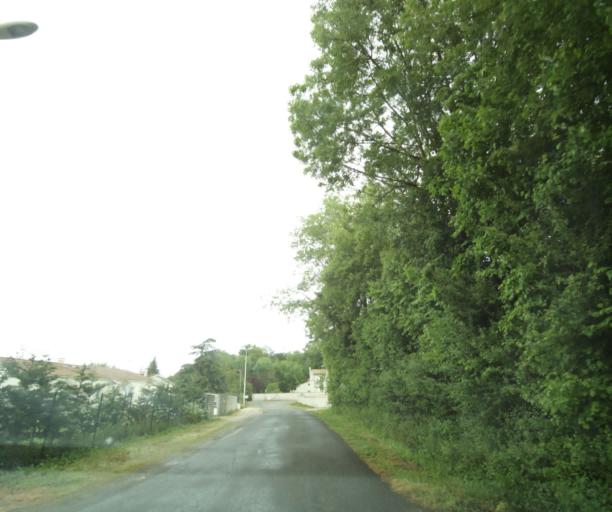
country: FR
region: Poitou-Charentes
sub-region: Departement de la Charente-Maritime
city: Cherac
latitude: 45.6832
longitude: -0.4898
